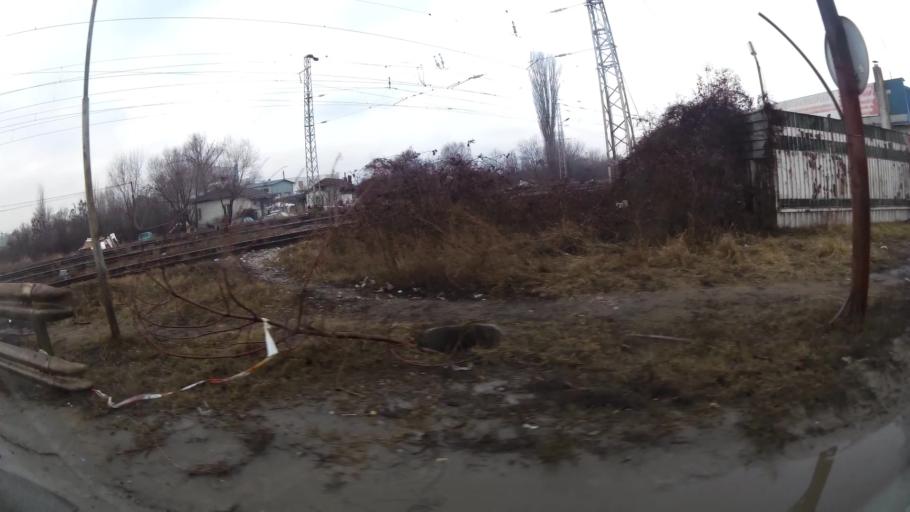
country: BG
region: Sofia-Capital
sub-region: Stolichna Obshtina
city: Sofia
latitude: 42.7324
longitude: 23.3437
